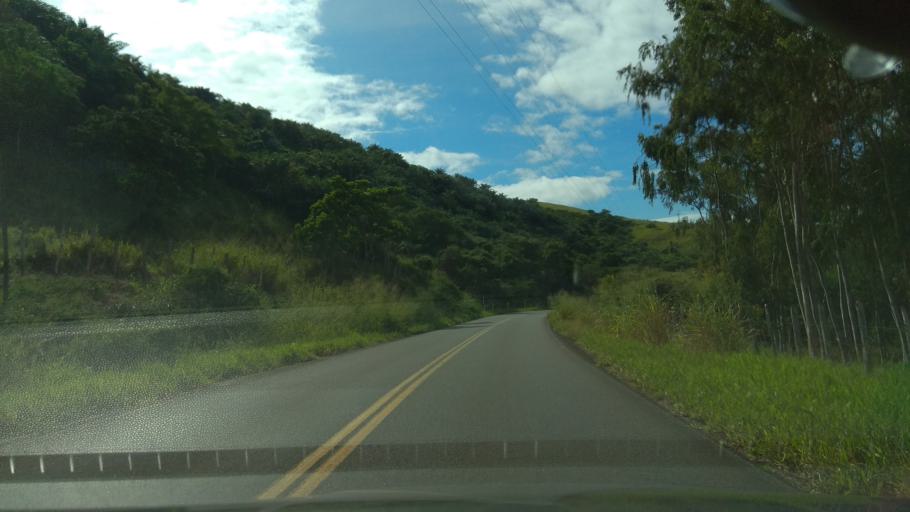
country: BR
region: Bahia
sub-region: Ubaira
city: Ubaira
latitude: -13.2601
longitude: -39.7034
